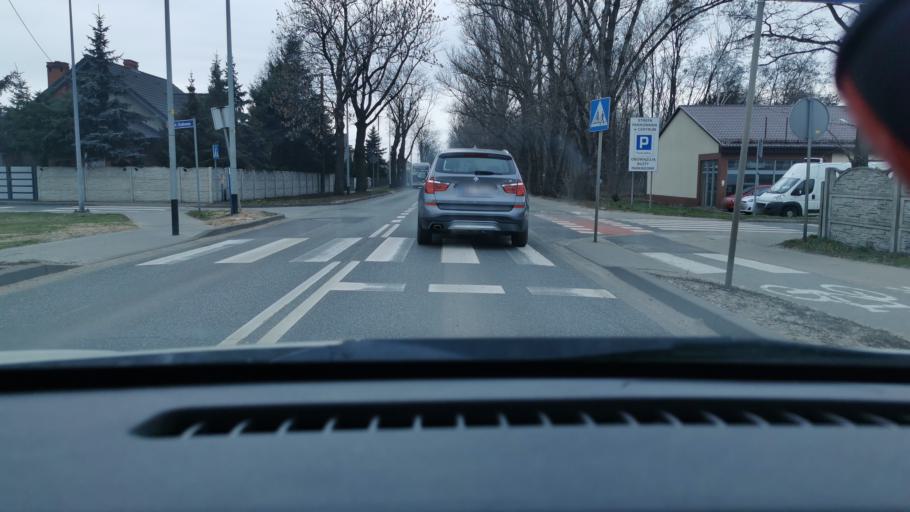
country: PL
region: Greater Poland Voivodeship
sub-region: Powiat ostrowski
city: Ostrow Wielkopolski
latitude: 51.6449
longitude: 17.8593
